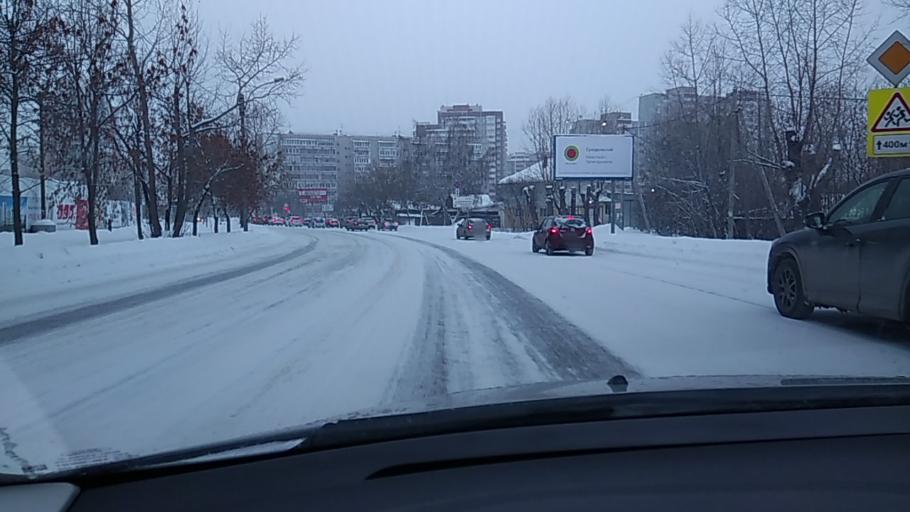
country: RU
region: Sverdlovsk
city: Sovkhoznyy
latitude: 56.8246
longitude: 60.5493
